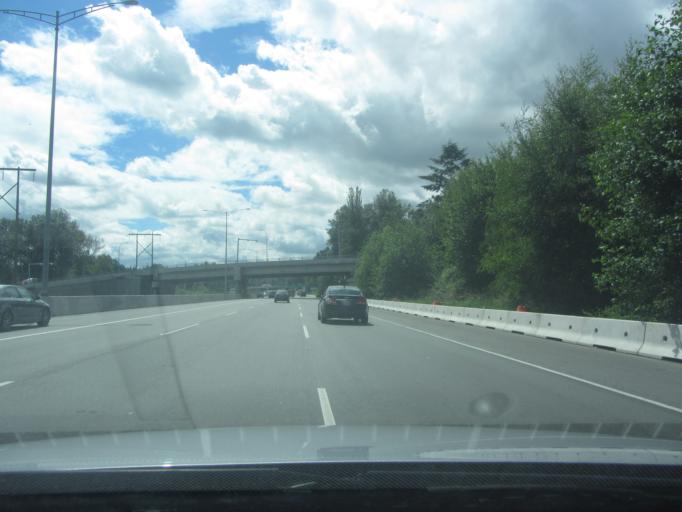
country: CA
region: British Columbia
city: Burnaby
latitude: 49.2511
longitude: -122.9746
